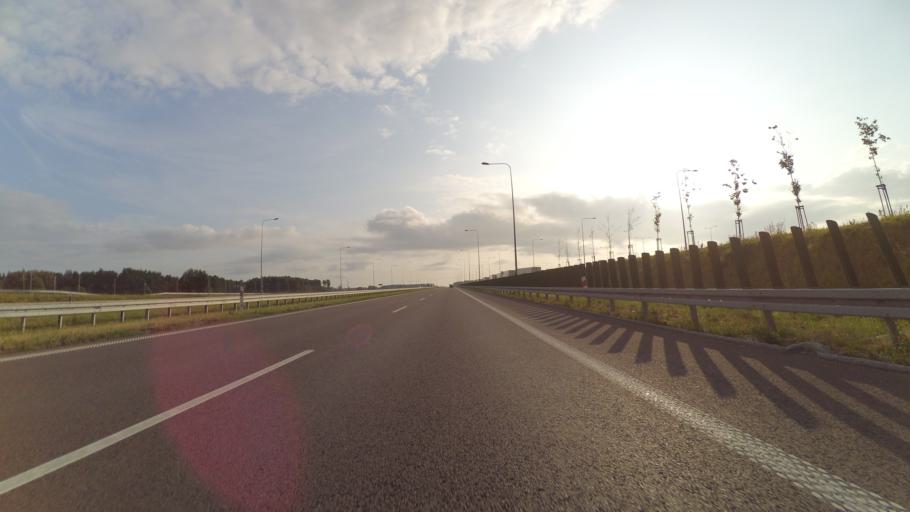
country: PL
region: Podlasie
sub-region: Powiat zambrowski
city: Rutki-Kossaki
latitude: 53.0577
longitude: 22.3964
